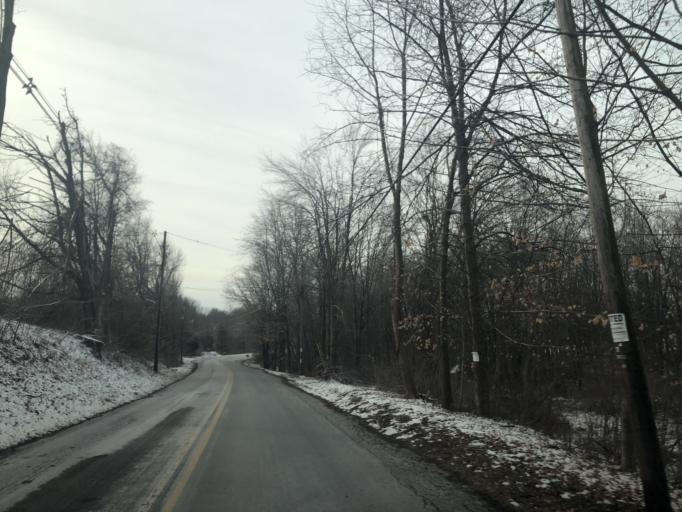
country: US
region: New Jersey
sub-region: Warren County
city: Belvidere
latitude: 40.9364
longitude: -75.0236
